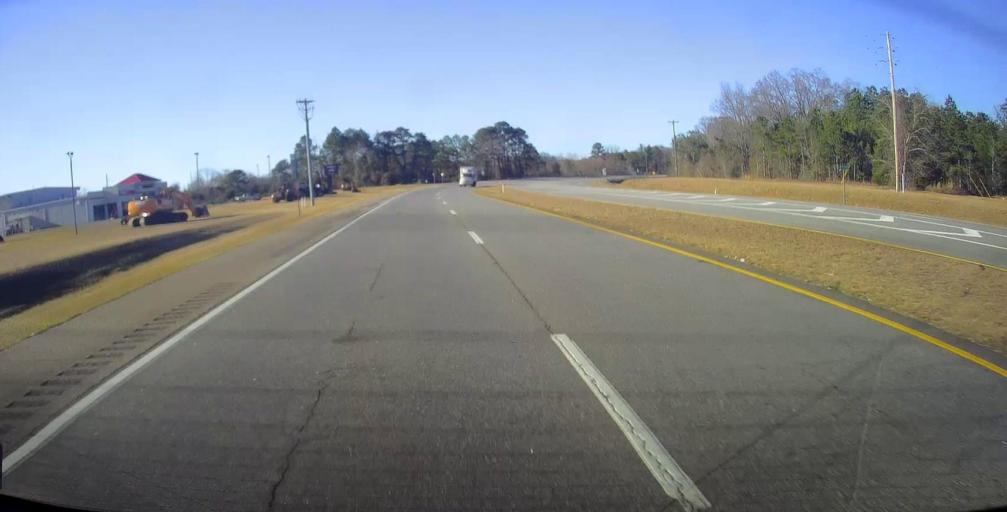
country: US
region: Georgia
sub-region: Sumter County
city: Americus
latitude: 31.9229
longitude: -84.2650
